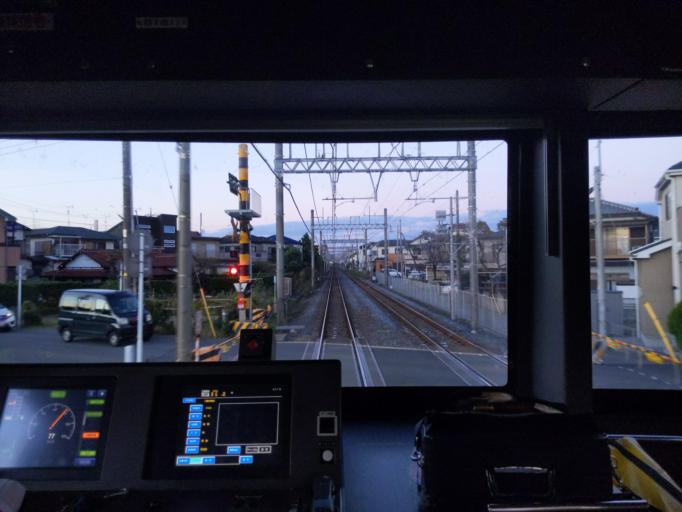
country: JP
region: Chiba
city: Kashiwa
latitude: 35.8442
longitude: 139.9646
